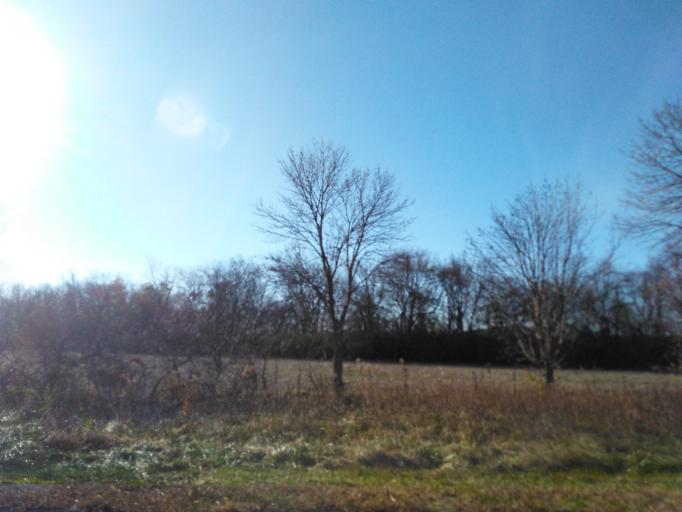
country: US
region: Illinois
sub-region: Madison County
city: Highland
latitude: 38.7864
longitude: -89.6777
